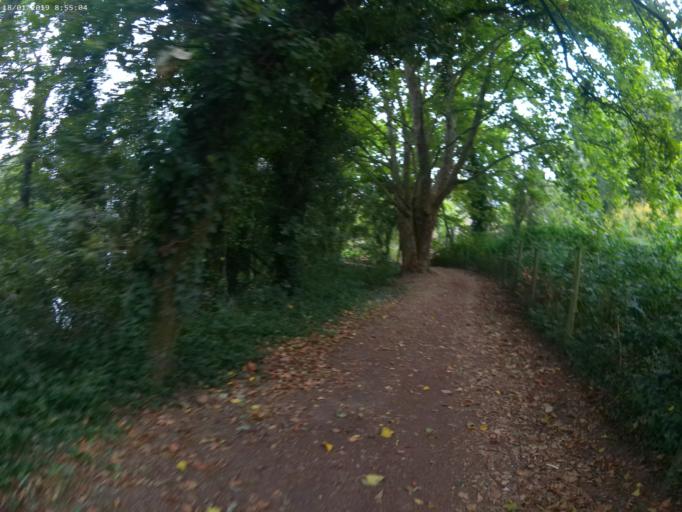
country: PT
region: Viana do Castelo
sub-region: Ponte da Barca
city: Ponte da Barca
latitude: 41.8065
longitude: -8.4352
